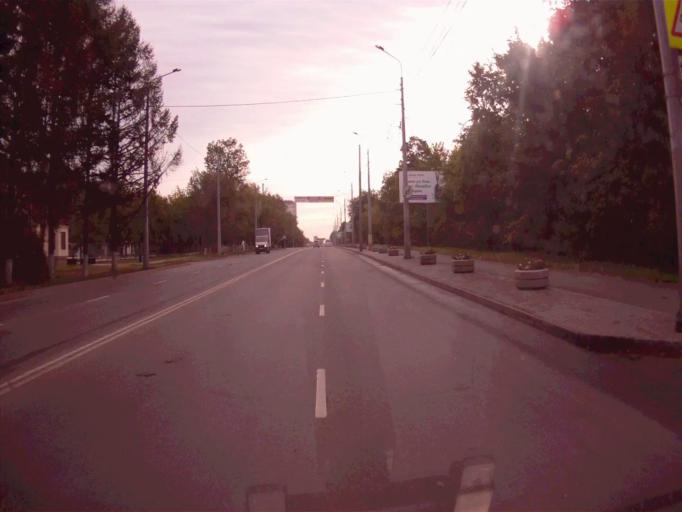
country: RU
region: Chelyabinsk
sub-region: Gorod Chelyabinsk
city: Chelyabinsk
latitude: 55.1471
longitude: 61.3562
